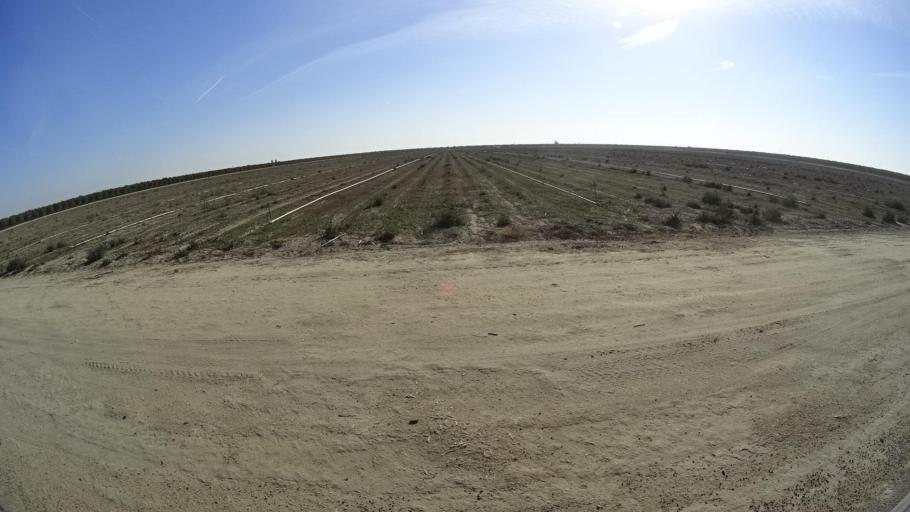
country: US
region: California
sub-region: Kern County
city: McFarland
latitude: 35.7032
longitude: -119.2893
